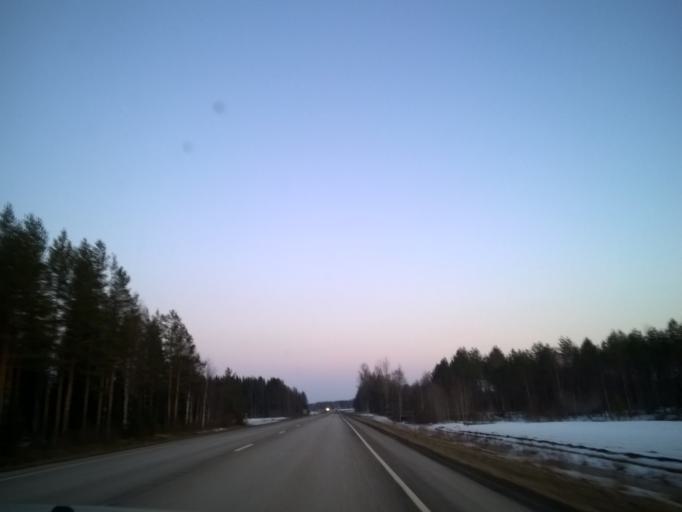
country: FI
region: Northern Ostrobothnia
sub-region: Nivala-Haapajaervi
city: Kaersaemaeki
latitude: 63.8413
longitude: 25.8558
